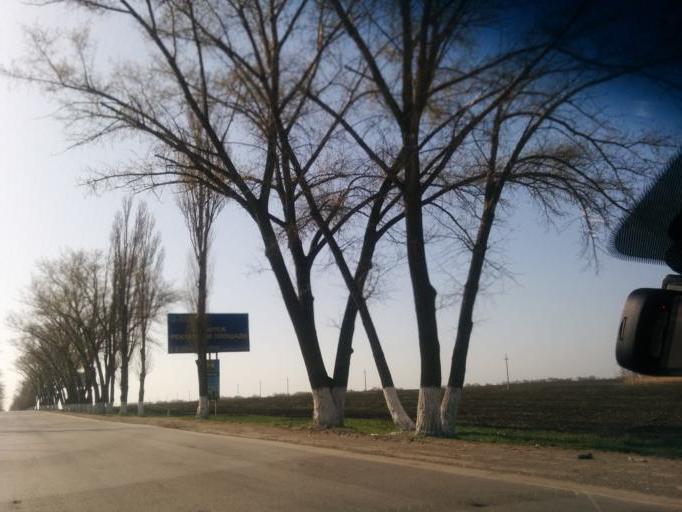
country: RU
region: Rostov
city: Mayskiy
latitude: 47.7120
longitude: 40.1295
